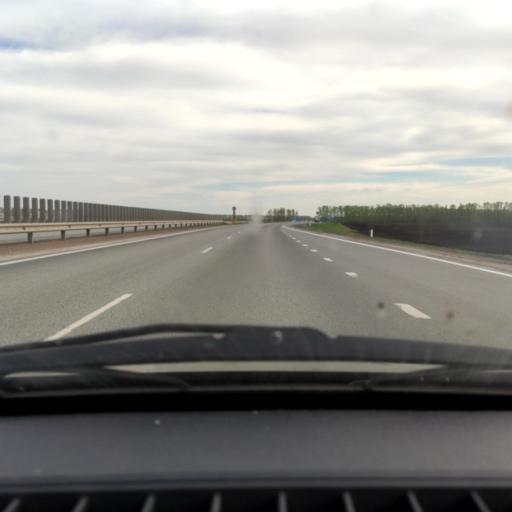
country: RU
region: Bashkortostan
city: Asanovo
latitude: 54.9567
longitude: 55.5854
